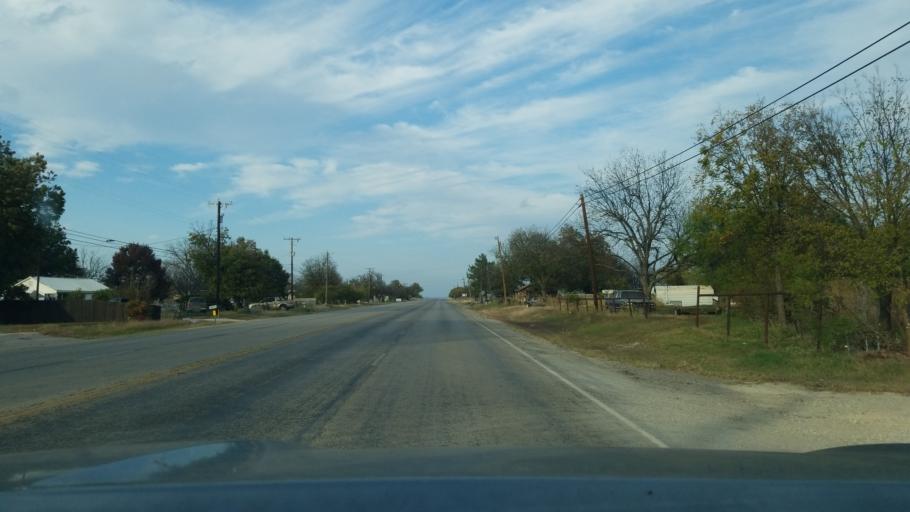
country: US
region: Texas
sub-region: Brown County
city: Early
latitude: 31.7659
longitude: -98.9551
